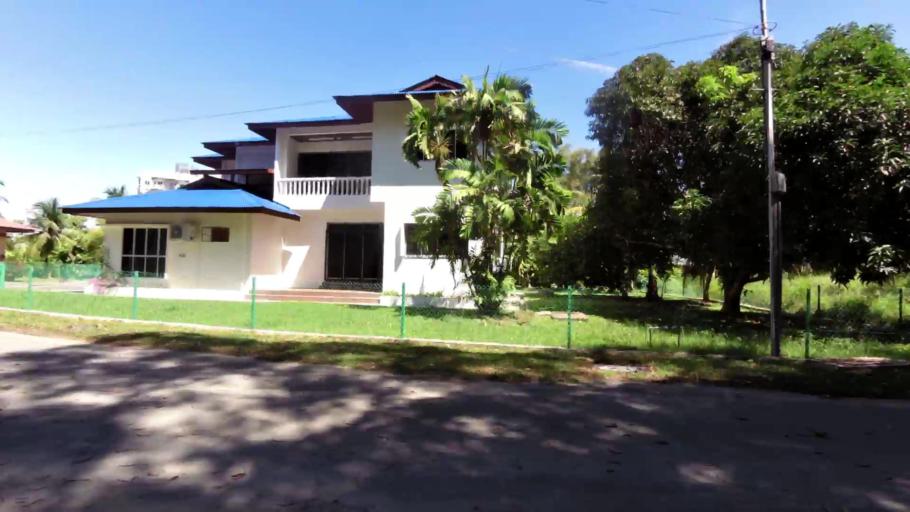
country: BN
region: Brunei and Muara
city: Bandar Seri Begawan
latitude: 5.0257
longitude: 115.0637
